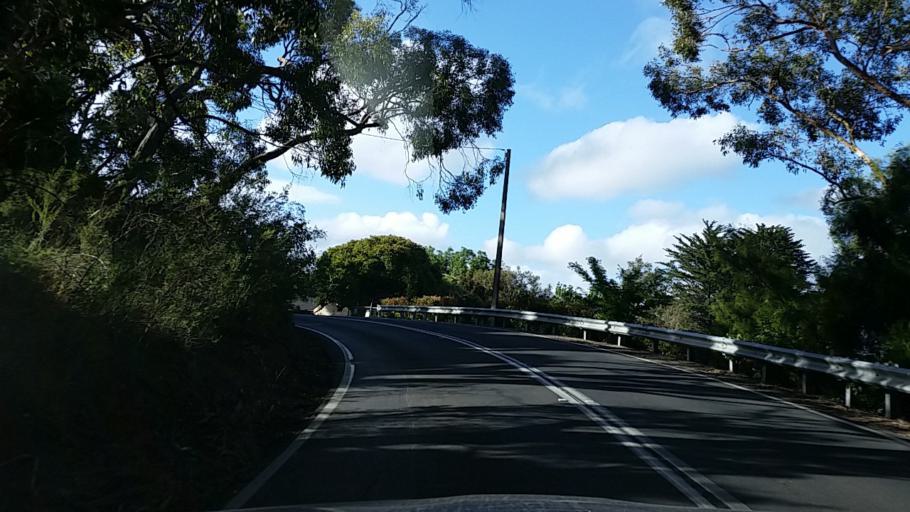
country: AU
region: South Australia
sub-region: Adelaide Hills
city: Stirling
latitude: -35.0216
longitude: 138.7541
